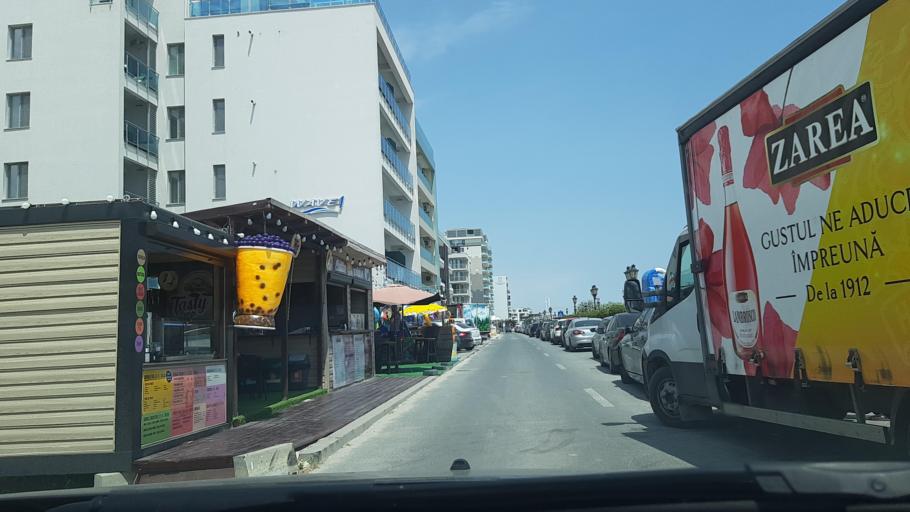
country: RO
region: Constanta
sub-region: Comuna Navodari
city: Navodari
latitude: 44.2915
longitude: 28.6236
